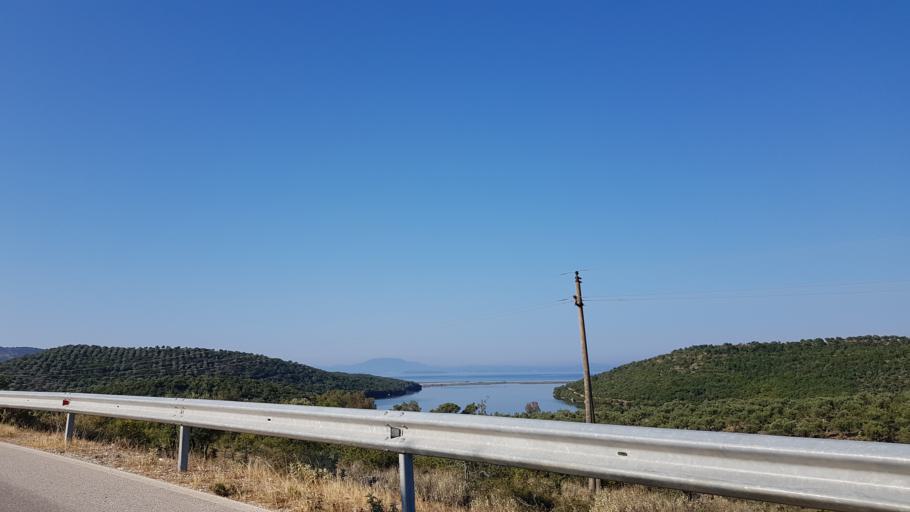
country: AL
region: Vlore
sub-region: Rrethi i Sarandes
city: Xarre
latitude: 39.7568
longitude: 20.0015
